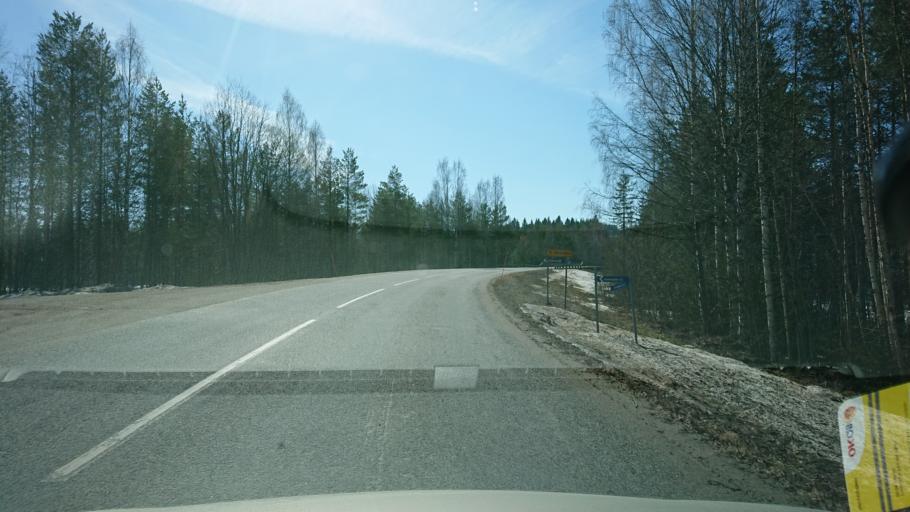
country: SE
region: Vaesterbotten
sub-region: Dorotea Kommun
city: Dorotea
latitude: 64.0063
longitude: 16.3052
